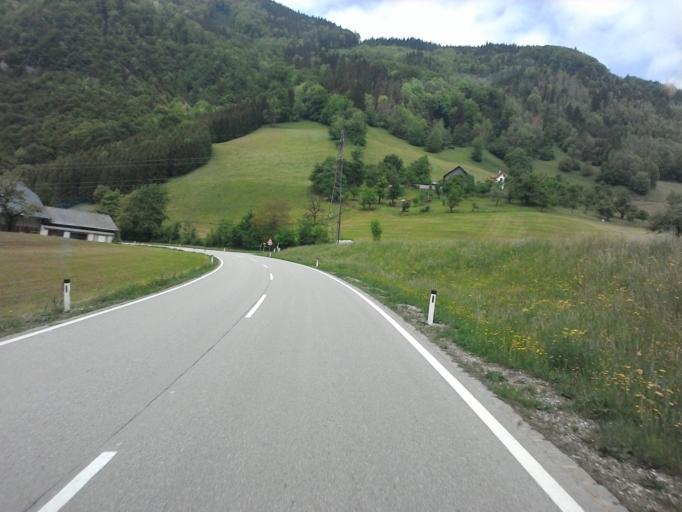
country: AT
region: Upper Austria
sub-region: Politischer Bezirk Steyr-Land
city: Weyer
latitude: 47.8561
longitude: 14.6416
